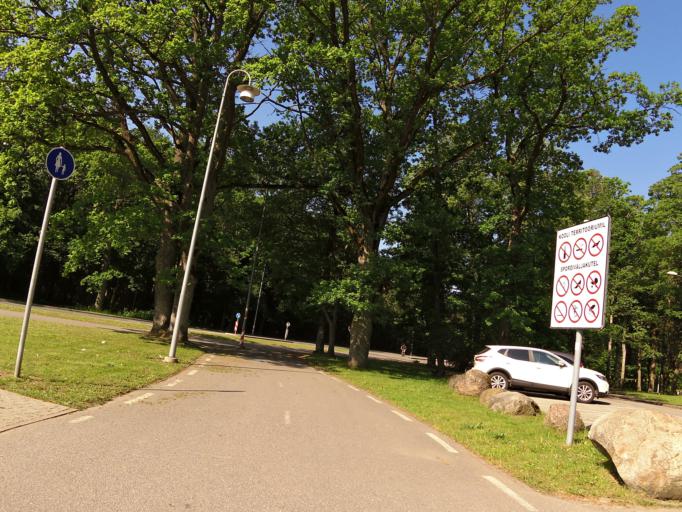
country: EE
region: Harju
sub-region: Saue vald
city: Laagri
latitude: 59.4307
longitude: 24.6511
